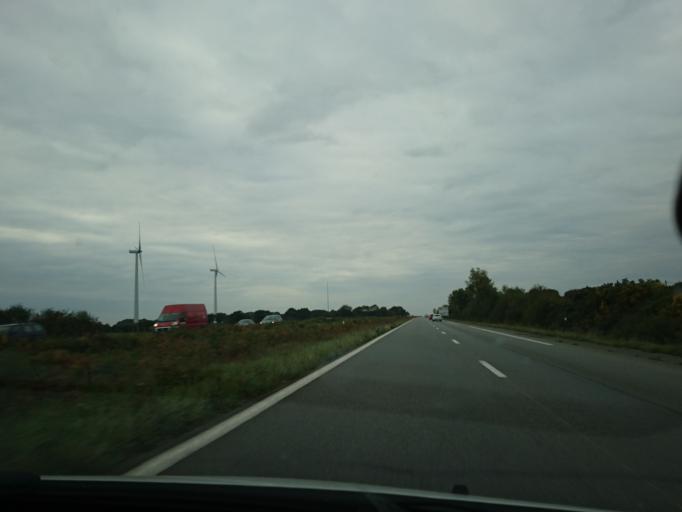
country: FR
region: Brittany
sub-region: Departement du Morbihan
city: Ambon
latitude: 47.5812
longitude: -2.5337
